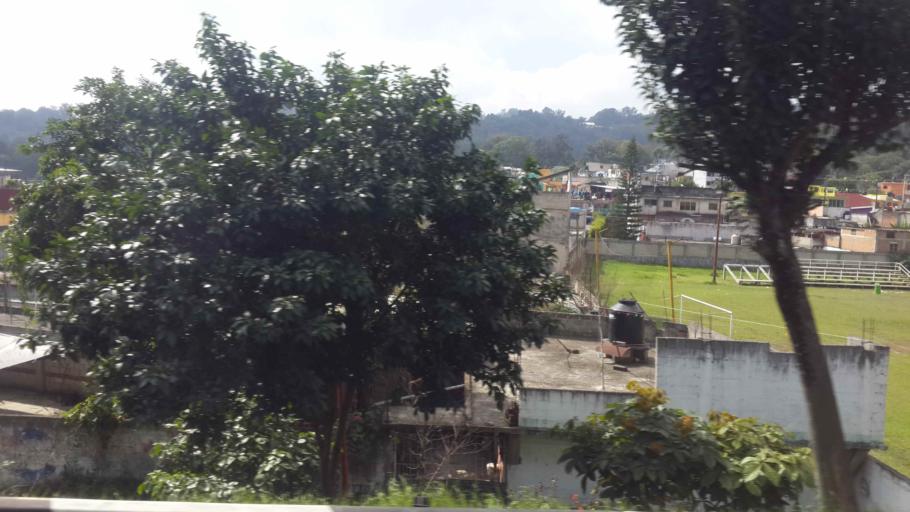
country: MX
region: Veracruz
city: Banderilla
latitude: 19.5882
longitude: -96.9351
